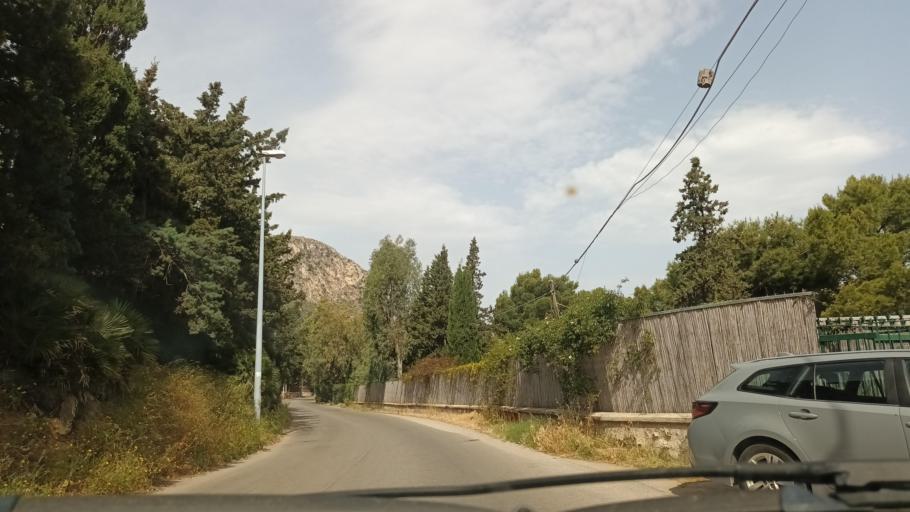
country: IT
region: Sicily
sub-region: Palermo
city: Santa Flavia
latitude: 38.1122
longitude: 13.5258
